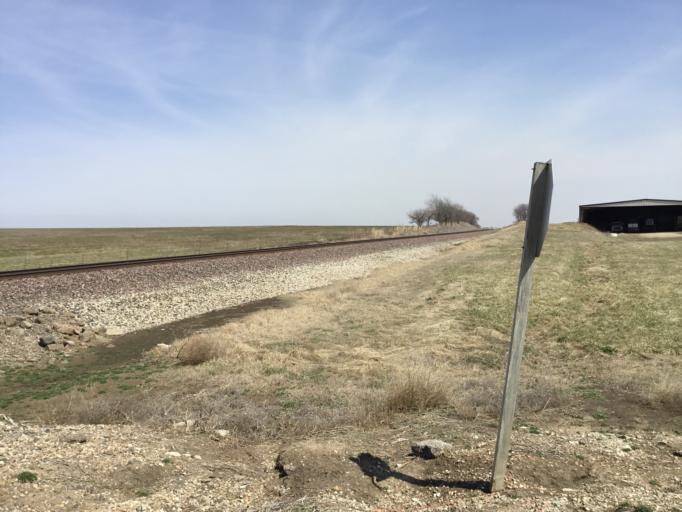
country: US
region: Kansas
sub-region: Lyon County
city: Emporia
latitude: 38.4631
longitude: -96.0780
